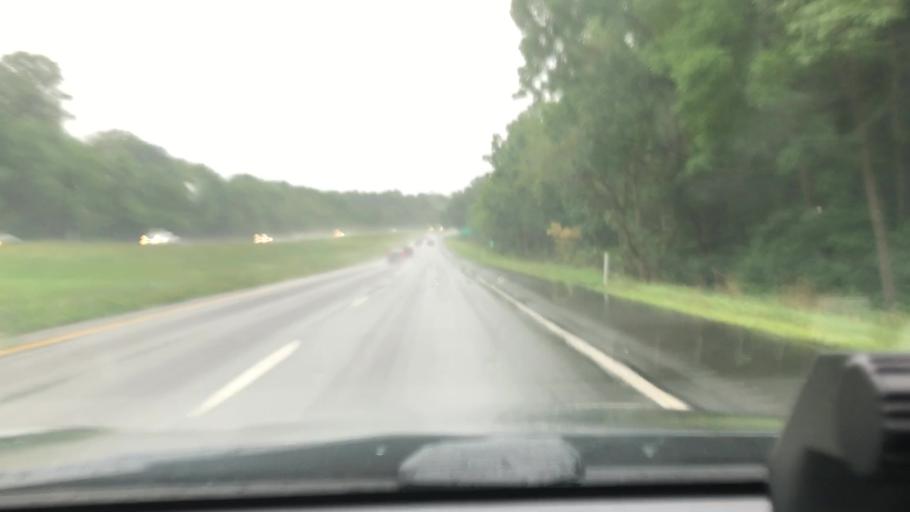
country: US
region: Pennsylvania
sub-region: Northampton County
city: Belfast
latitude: 40.7969
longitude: -75.2928
